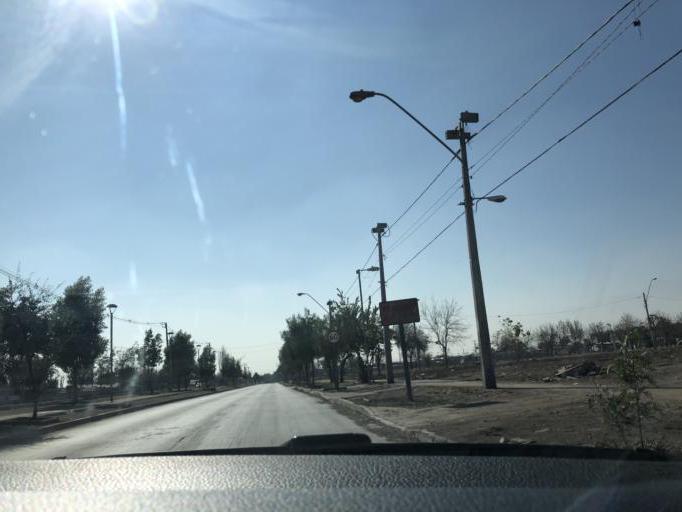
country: CL
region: Santiago Metropolitan
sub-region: Provincia de Santiago
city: La Pintana
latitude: -33.6315
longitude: -70.6294
